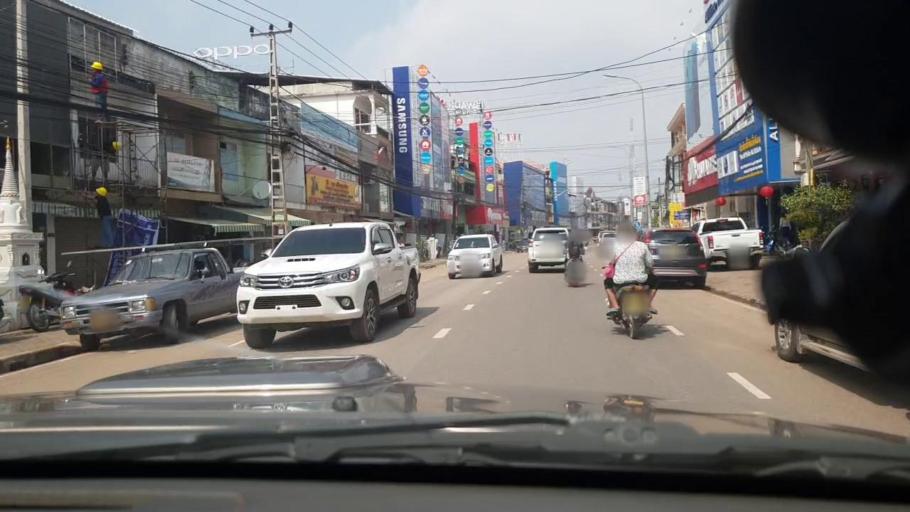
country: LA
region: Vientiane
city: Vientiane
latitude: 17.9640
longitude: 102.6200
